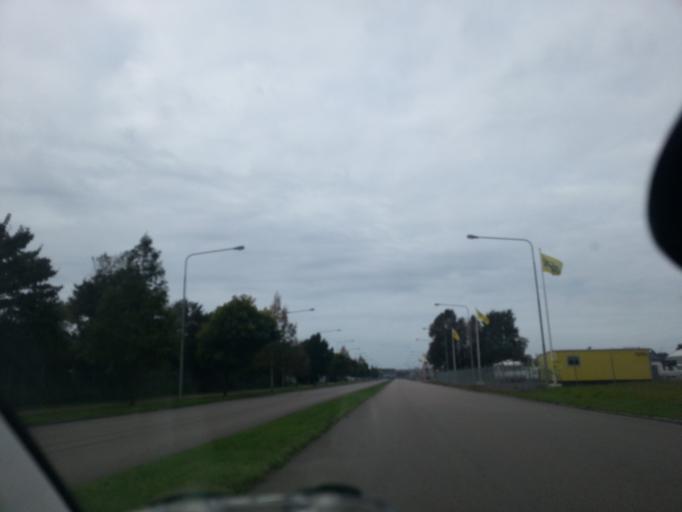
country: SE
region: Skane
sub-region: Landskrona
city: Landskrona
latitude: 55.8664
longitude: 12.8575
